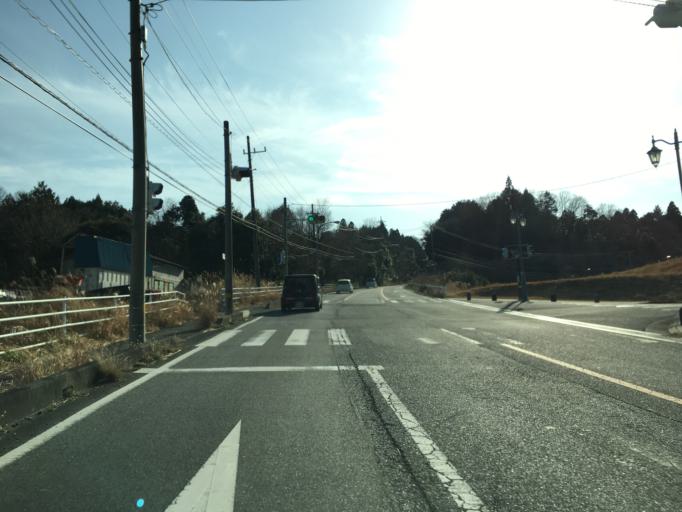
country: JP
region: Ibaraki
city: Takahagi
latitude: 36.7325
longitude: 140.6866
